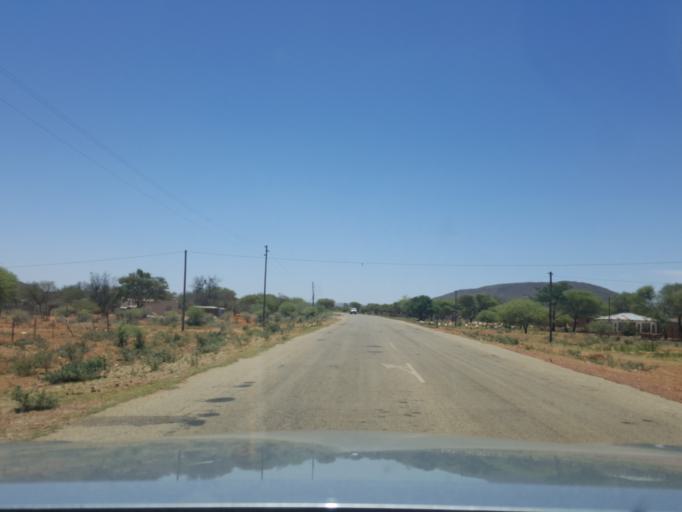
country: BW
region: South East
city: Ramotswa
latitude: -24.9745
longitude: 25.8966
